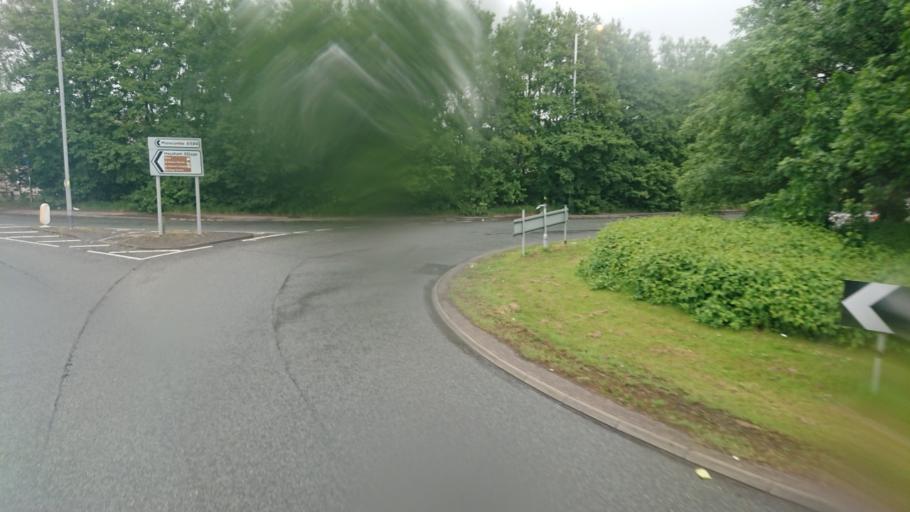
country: GB
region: England
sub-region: Lancashire
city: Morecambe
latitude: 54.0353
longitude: -2.8959
